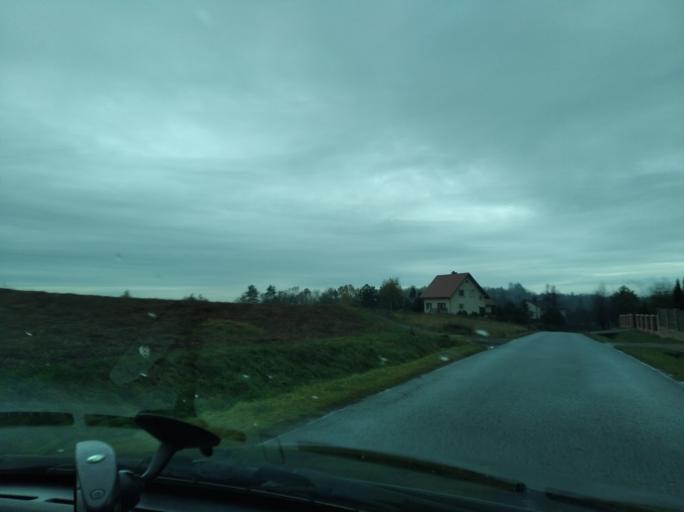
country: PL
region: Subcarpathian Voivodeship
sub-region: Powiat rzeszowski
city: Tyczyn
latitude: 49.9325
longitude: 22.0307
